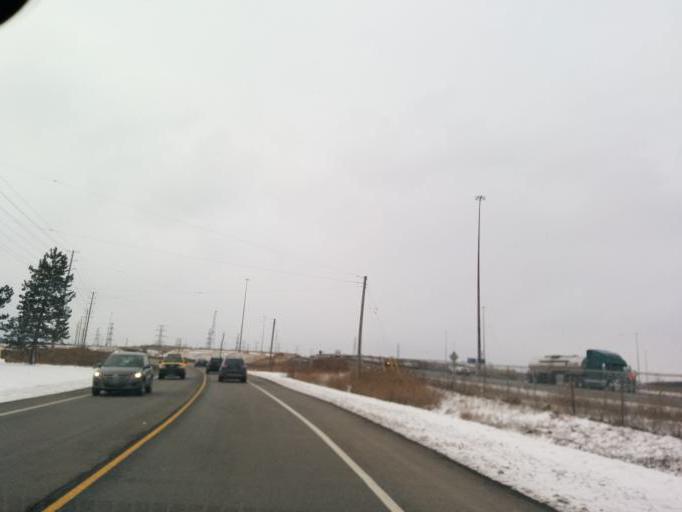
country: CA
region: Ontario
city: Mississauga
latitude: 43.5239
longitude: -79.7189
